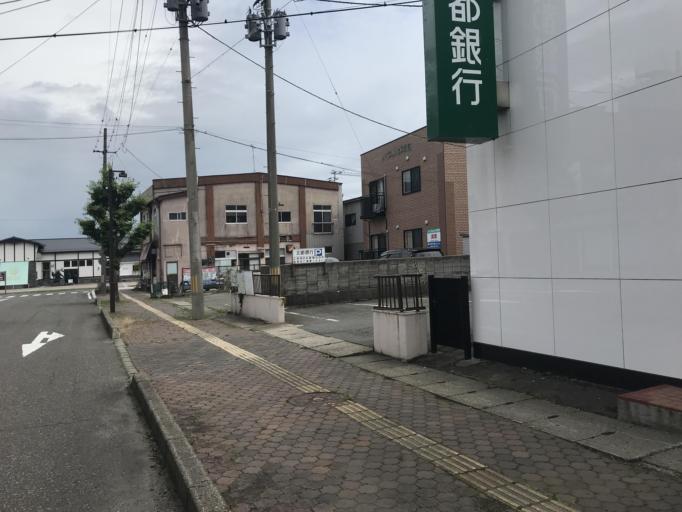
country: JP
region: Akita
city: Tenno
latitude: 39.8853
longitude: 139.8476
